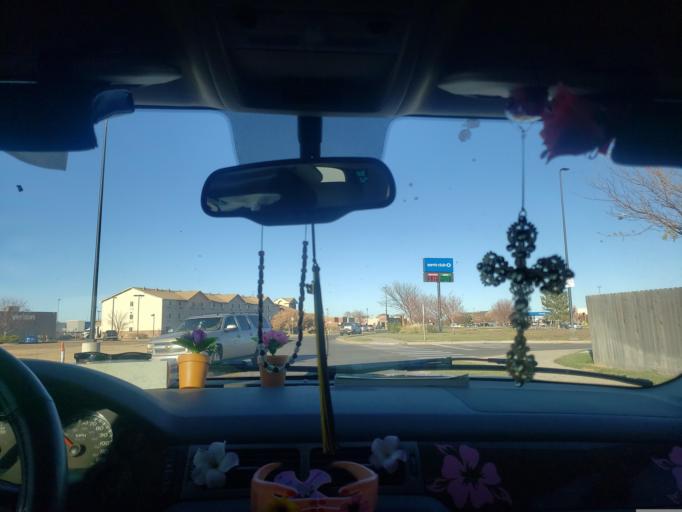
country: US
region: Kansas
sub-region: Finney County
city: Garden City
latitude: 37.9827
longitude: -100.8357
